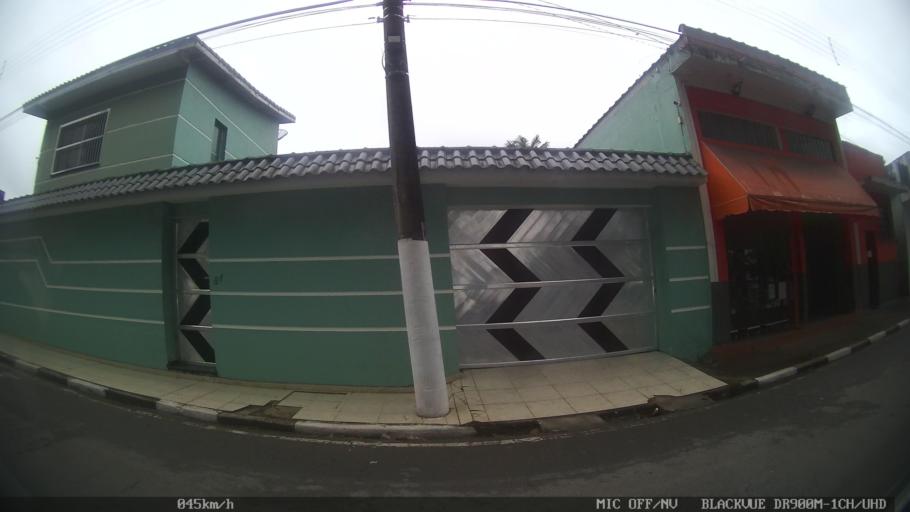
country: BR
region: Sao Paulo
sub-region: Juquia
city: Juquia
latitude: -24.3298
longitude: -47.6312
